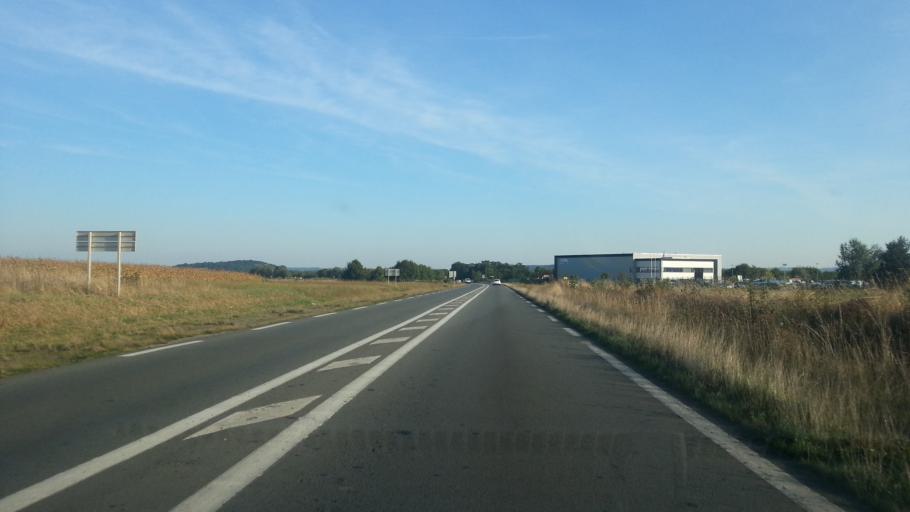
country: FR
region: Picardie
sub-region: Departement de l'Oise
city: Allonne
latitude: 49.4299
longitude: 2.1255
